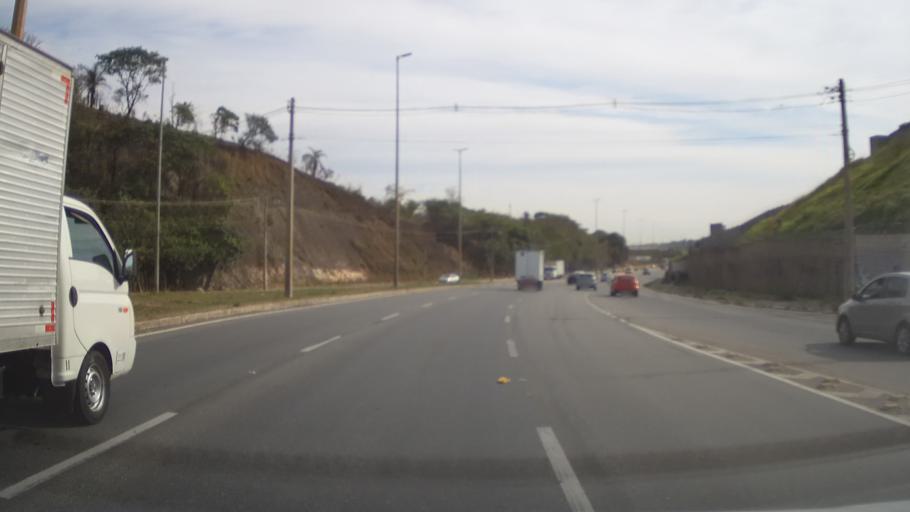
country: BR
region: Minas Gerais
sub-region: Contagem
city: Contagem
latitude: -19.9157
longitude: -44.0545
